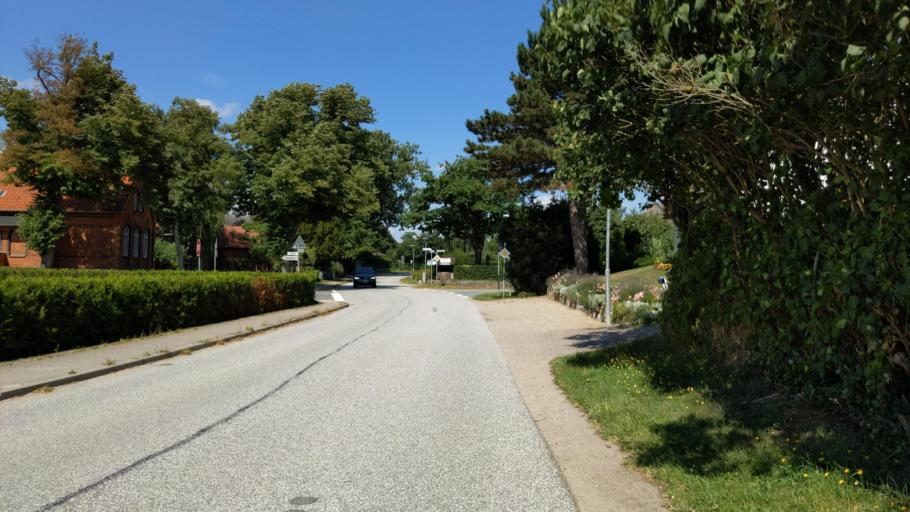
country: DE
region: Schleswig-Holstein
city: Krummesse
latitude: 53.8091
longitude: 10.6835
